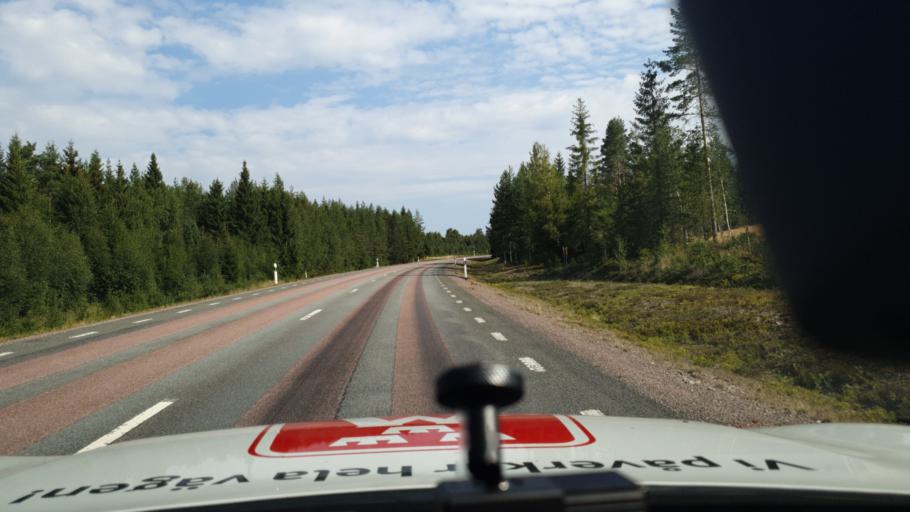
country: SE
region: Dalarna
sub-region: Malung-Saelens kommun
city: Malung
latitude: 60.5111
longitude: 13.4345
